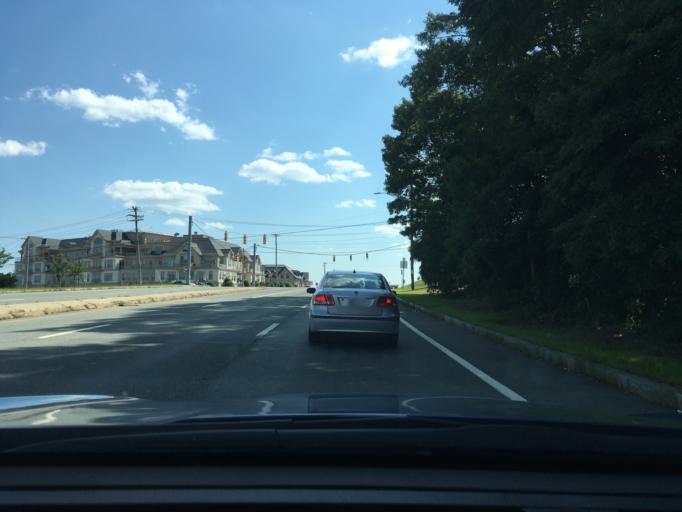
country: US
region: Rhode Island
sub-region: Providence County
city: Cranston
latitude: 41.7594
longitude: -71.4600
